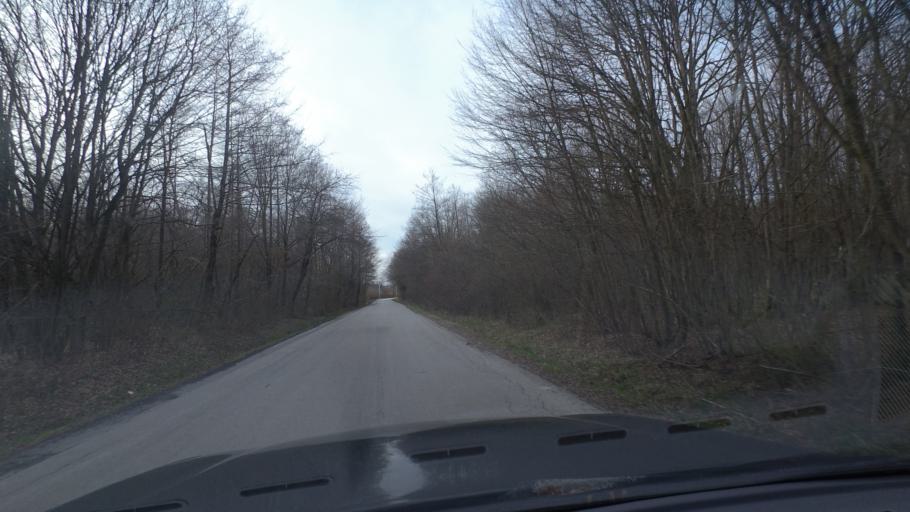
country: HR
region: Grad Zagreb
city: Horvati
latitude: 45.7069
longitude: 15.8284
